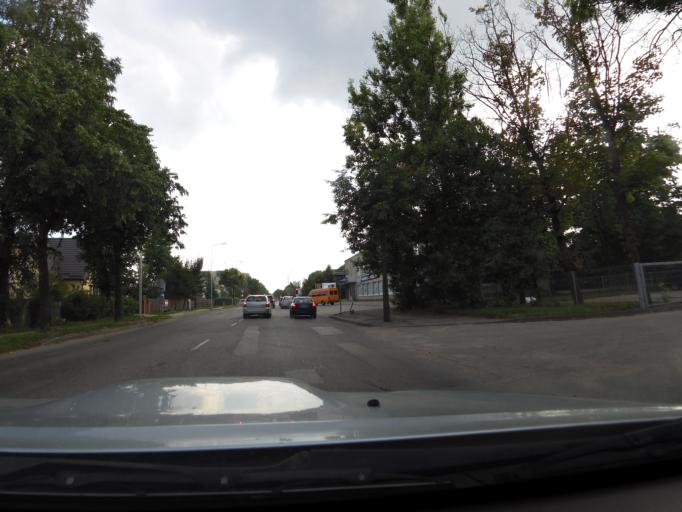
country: LT
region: Siauliu apskritis
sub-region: Siauliai
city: Siauliai
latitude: 55.9496
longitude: 23.3132
